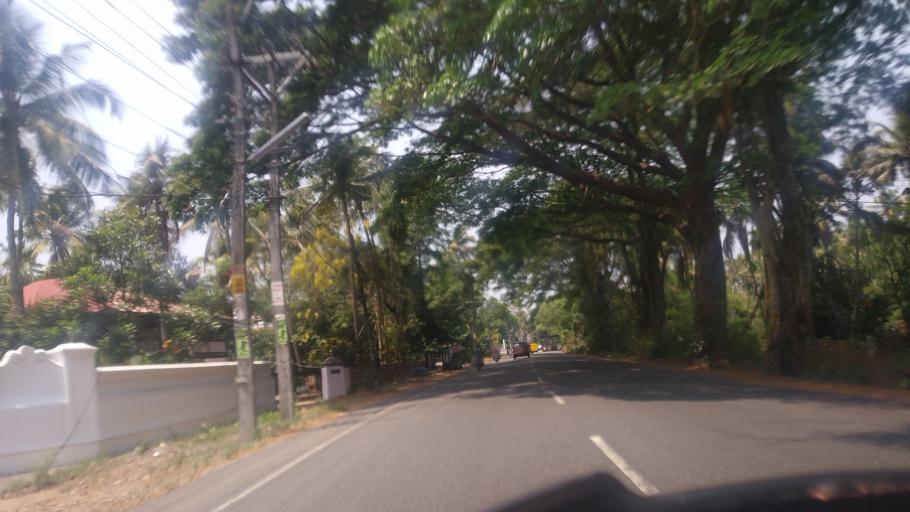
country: IN
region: Kerala
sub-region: Thrissur District
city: Kodungallur
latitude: 10.2549
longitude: 76.1849
